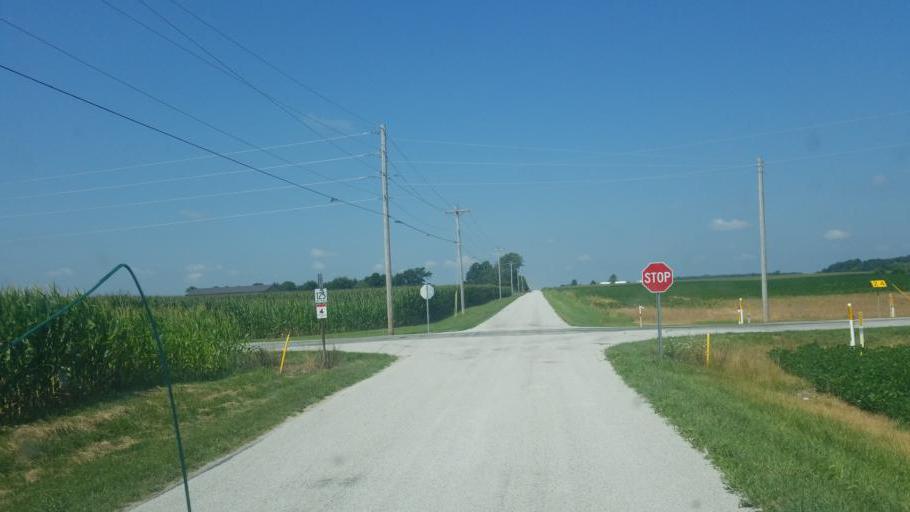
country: US
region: Ohio
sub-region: Hardin County
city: Kenton
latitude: 40.7033
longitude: -83.6725
